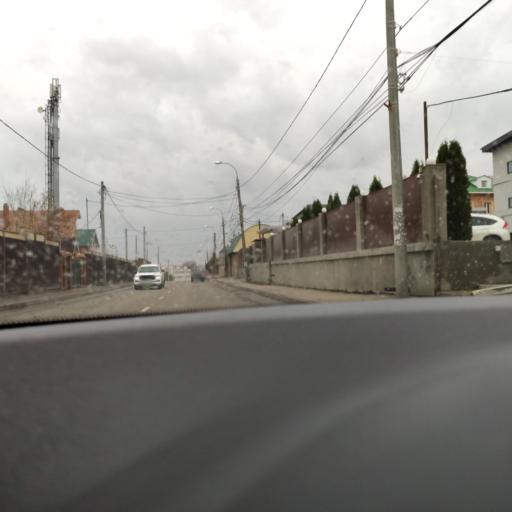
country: RU
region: Samara
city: Samara
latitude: 53.2669
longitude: 50.2029
